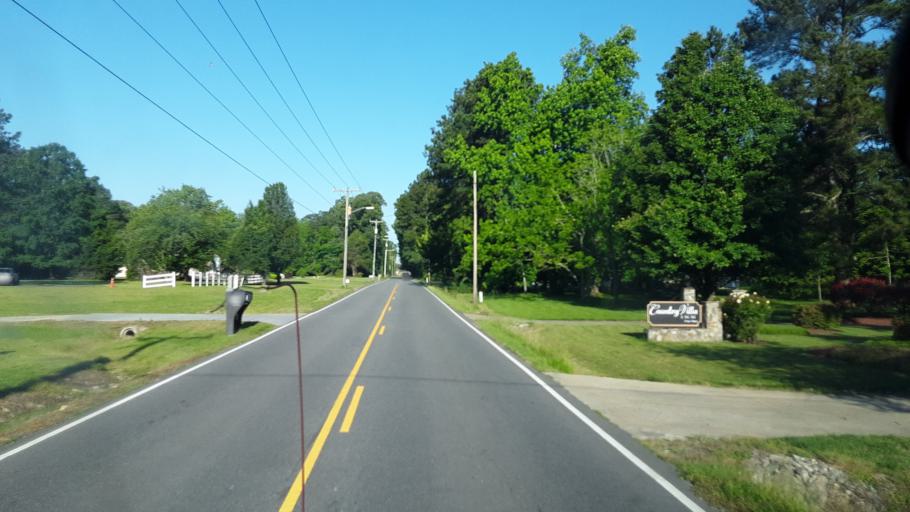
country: US
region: Virginia
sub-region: City of Virginia Beach
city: Virginia Beach
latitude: 36.7206
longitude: -76.0363
